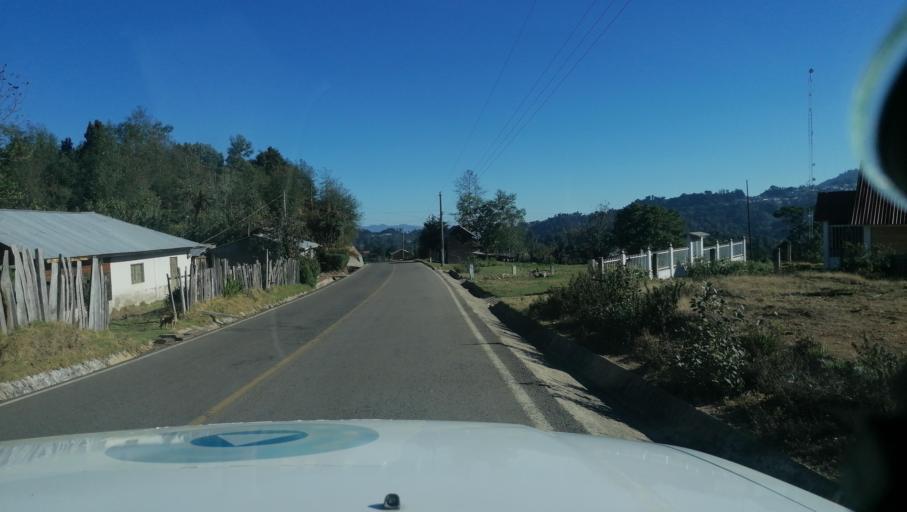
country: MX
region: Chiapas
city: Motozintla de Mendoza
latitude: 15.2407
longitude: -92.2304
